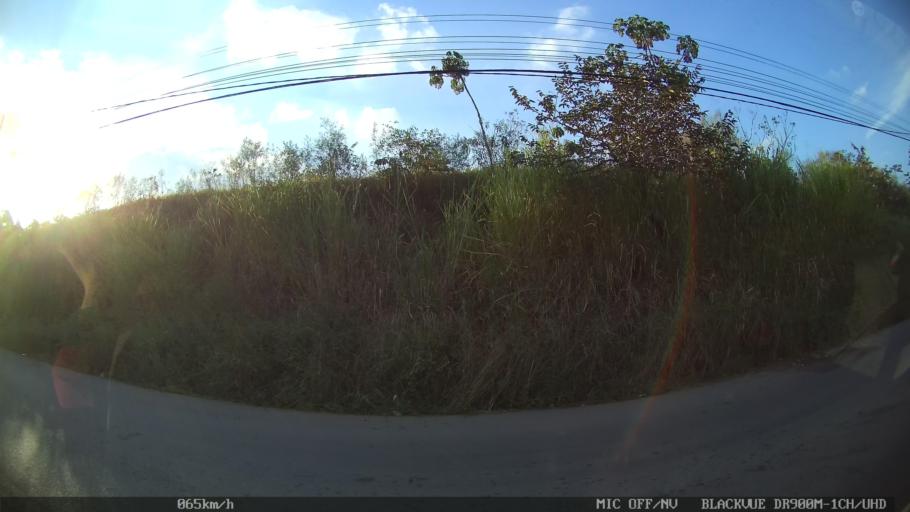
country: BR
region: Sao Paulo
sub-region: Hortolandia
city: Hortolandia
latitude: -22.8638
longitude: -47.1887
